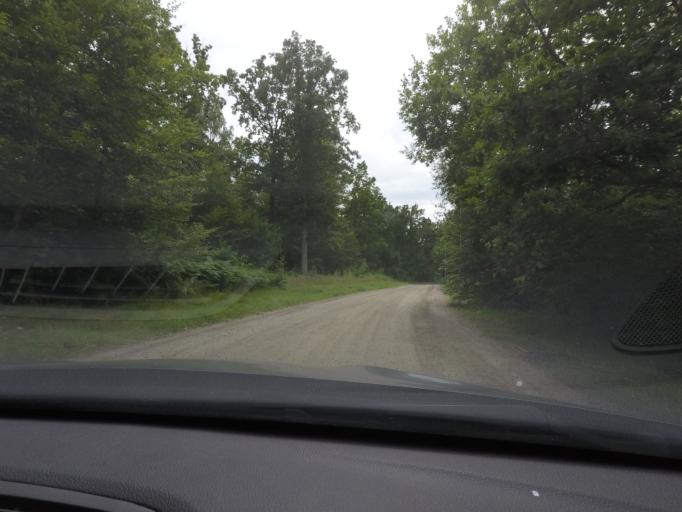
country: SE
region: Skane
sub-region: Osby Kommun
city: Osby
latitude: 56.3579
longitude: 13.9966
